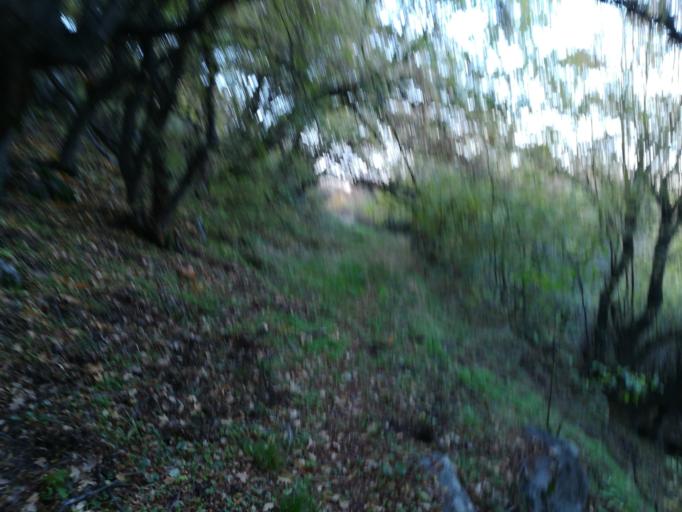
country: BG
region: Khaskovo
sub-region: Obshtina Mineralni Bani
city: Mineralni Bani
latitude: 41.9804
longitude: 25.2390
